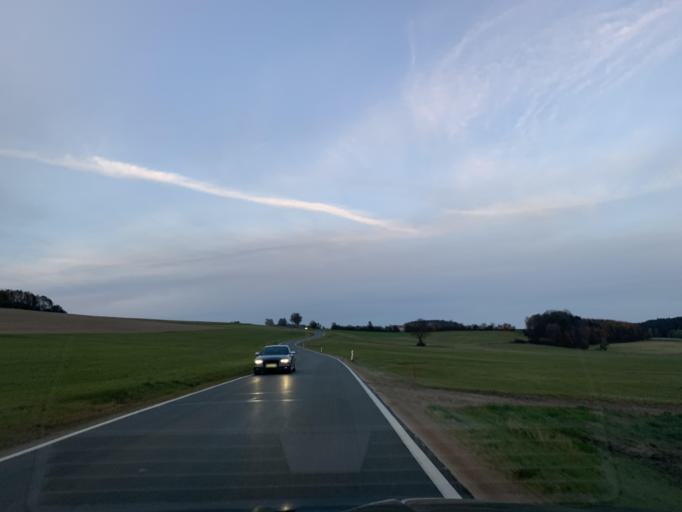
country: DE
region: Bavaria
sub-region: Upper Palatinate
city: Bach
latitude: 49.3960
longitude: 12.4041
